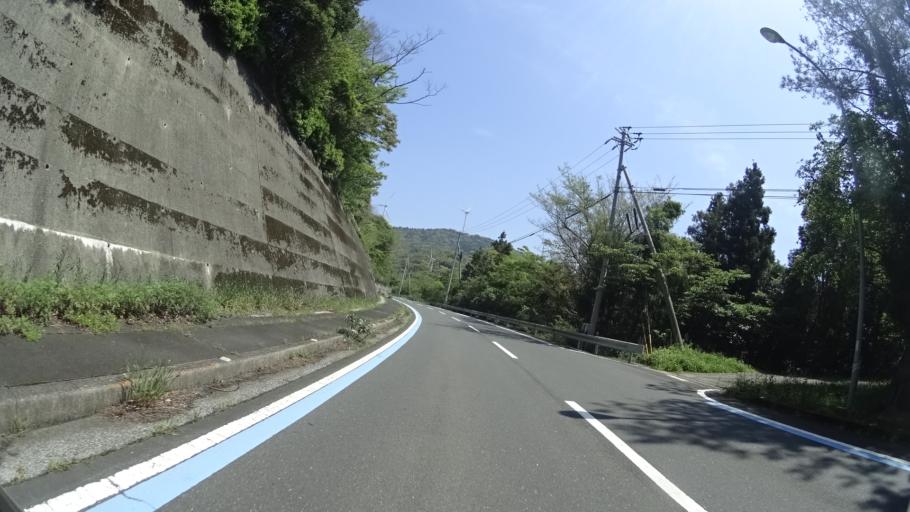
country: JP
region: Ehime
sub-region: Nishiuwa-gun
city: Ikata-cho
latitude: 33.4174
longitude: 132.1824
